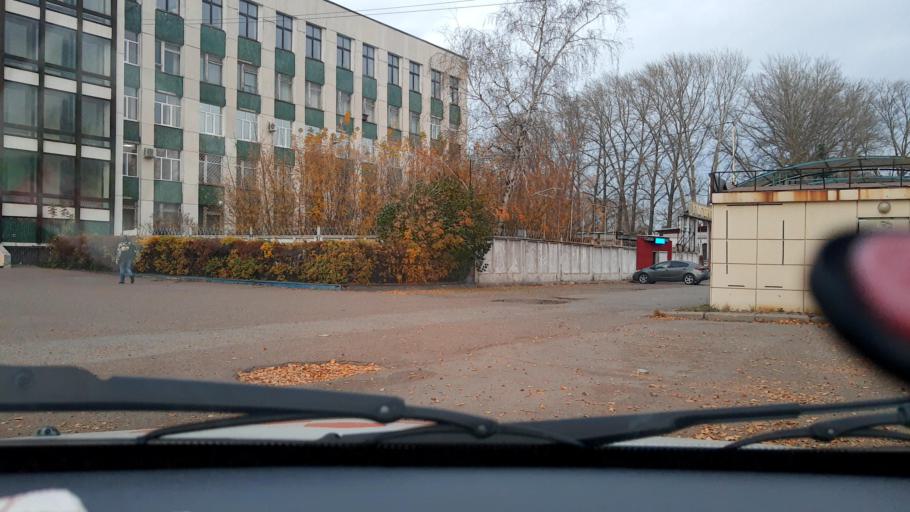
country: RU
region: Bashkortostan
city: Ufa
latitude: 54.8038
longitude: 56.0972
